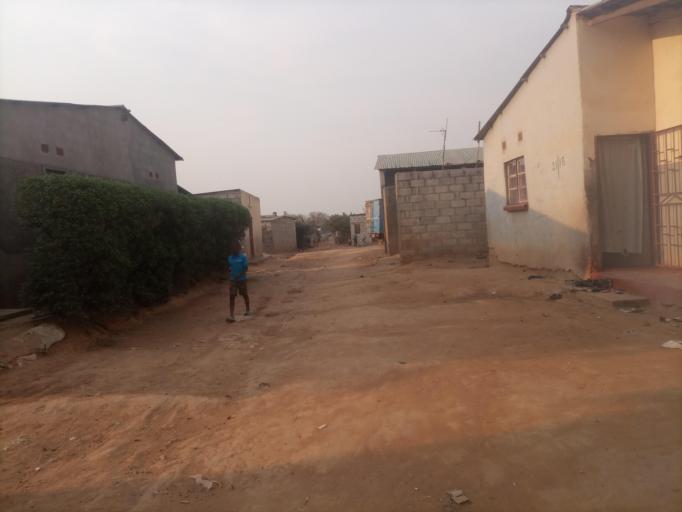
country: ZM
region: Lusaka
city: Lusaka
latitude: -15.3952
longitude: 28.3776
